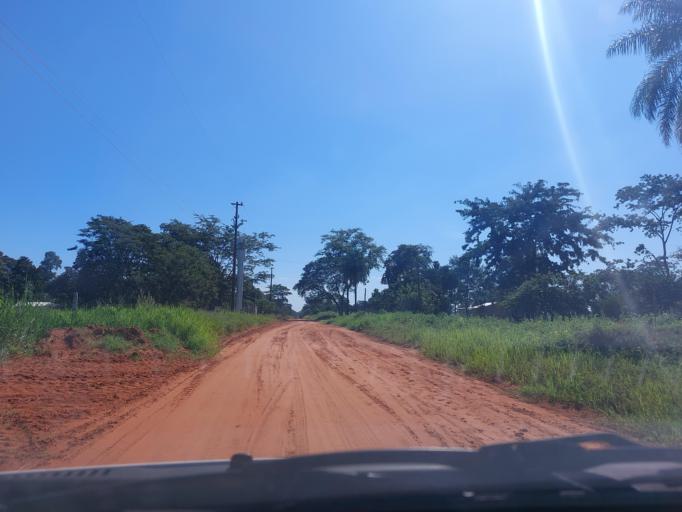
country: PY
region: San Pedro
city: Lima
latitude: -24.1539
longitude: -56.0114
